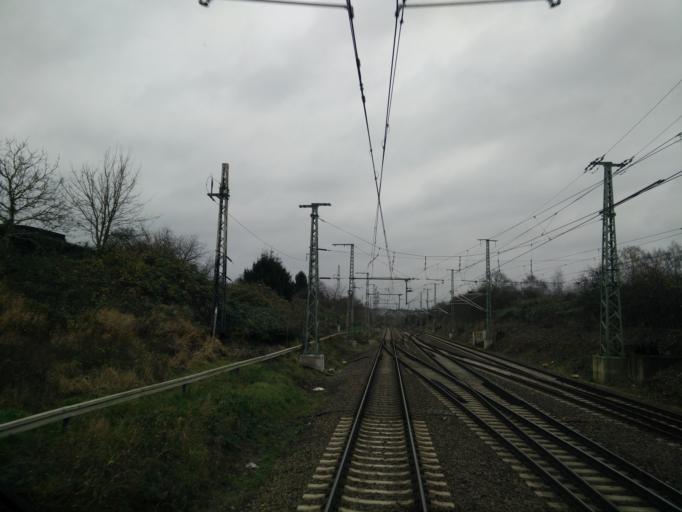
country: DE
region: Mecklenburg-Vorpommern
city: Bad Kleinen
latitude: 53.7720
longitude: 11.4792
